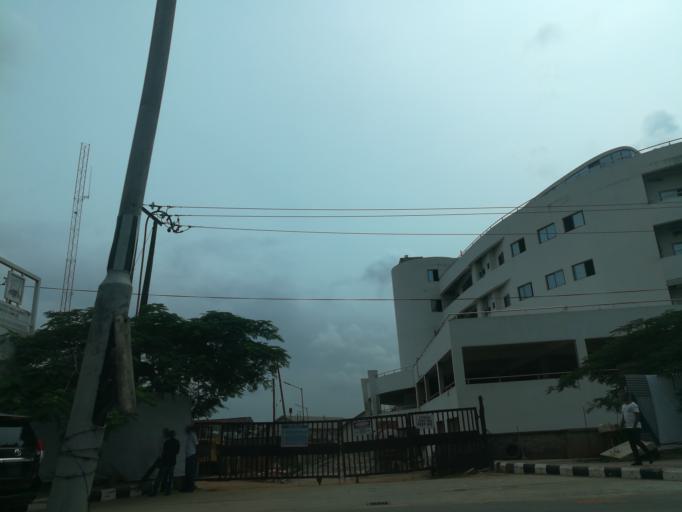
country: NG
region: Lagos
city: Ikeja
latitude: 6.6168
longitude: 3.3622
